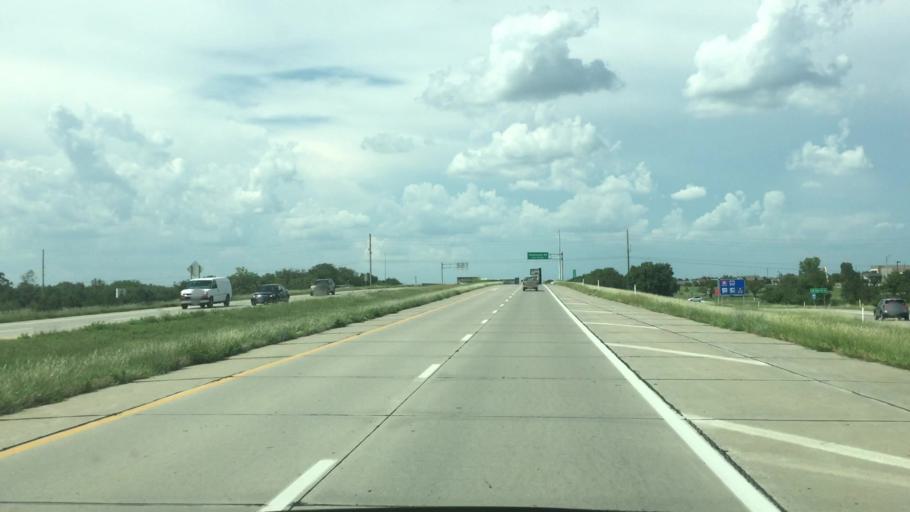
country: US
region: Kansas
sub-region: Butler County
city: Andover
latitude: 37.7208
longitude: -97.1994
